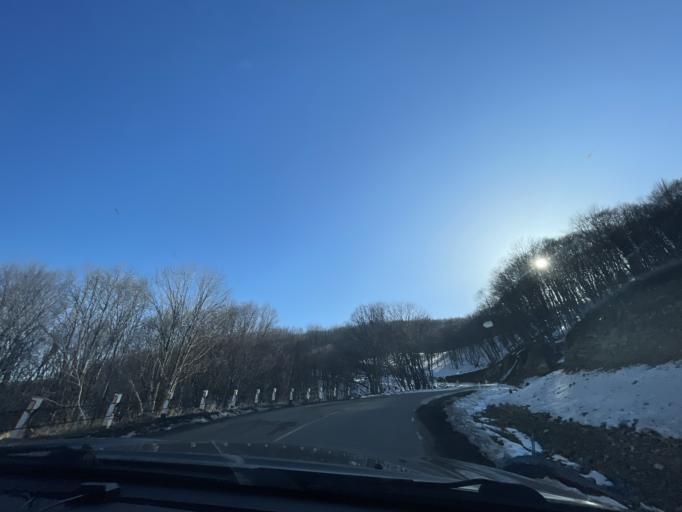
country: GE
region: Kvemo Kartli
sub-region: Tetri Tsqaro
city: Manglisi
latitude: 41.7729
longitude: 44.5070
